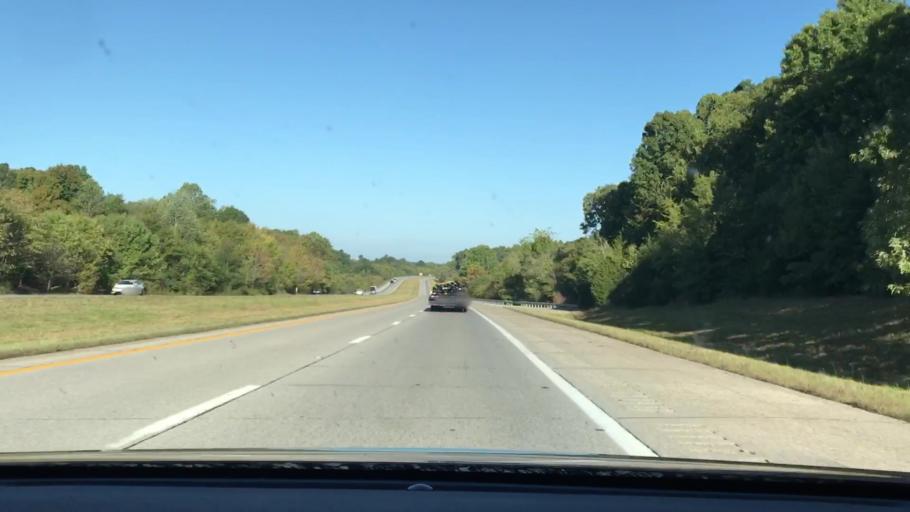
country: US
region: Kentucky
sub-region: Lyon County
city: Eddyville
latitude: 37.0234
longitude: -87.9898
